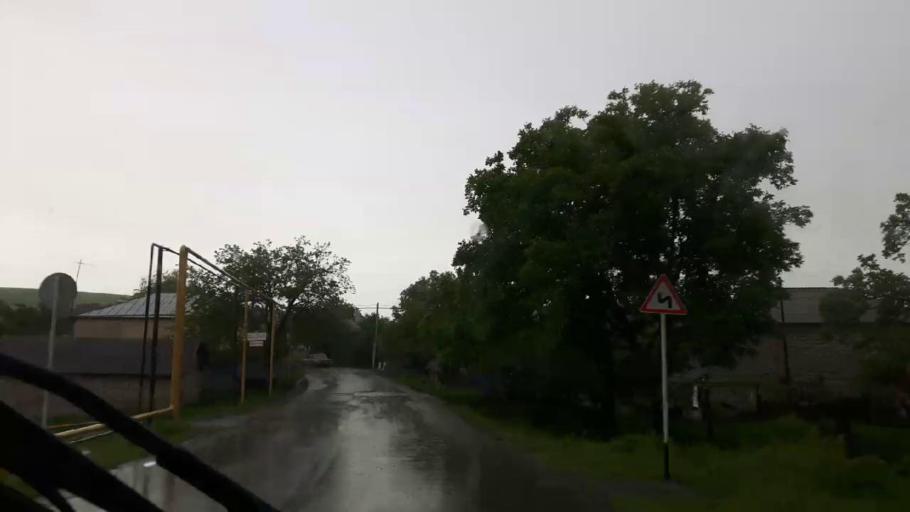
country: GE
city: Agara
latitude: 42.0130
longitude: 43.8521
